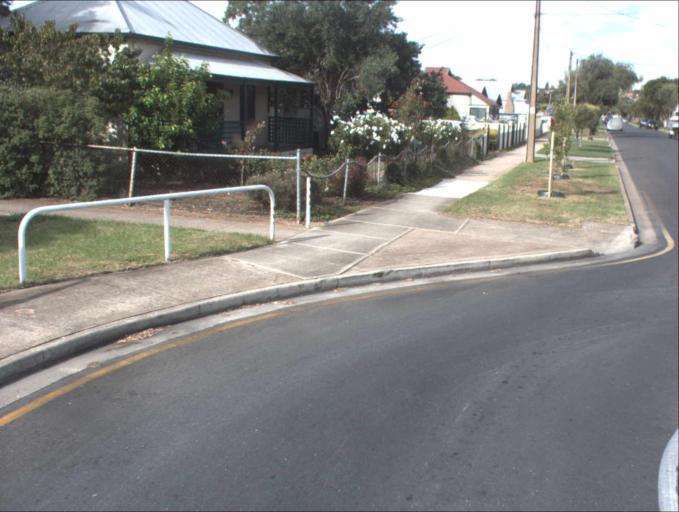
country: AU
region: South Australia
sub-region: Port Adelaide Enfield
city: Blair Athol
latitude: -34.8664
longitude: 138.5874
